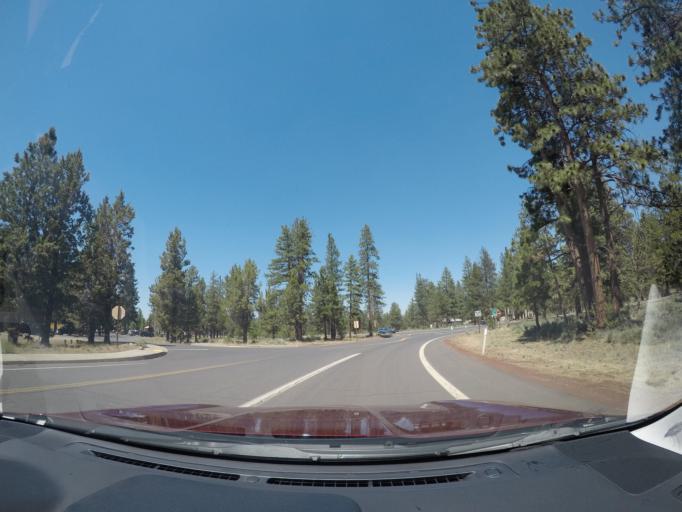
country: US
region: Oregon
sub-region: Deschutes County
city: Sisters
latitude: 44.2925
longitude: -121.5575
